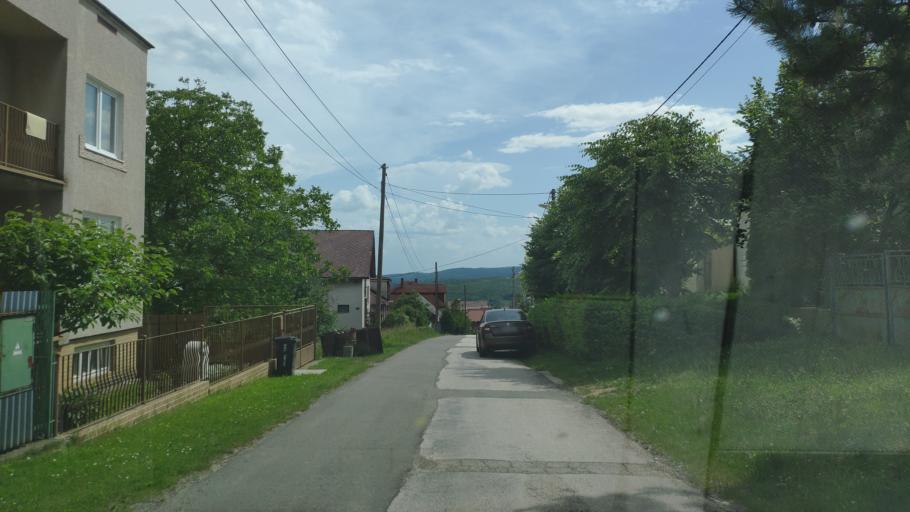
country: SK
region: Kosicky
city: Medzev
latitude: 48.7130
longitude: 20.9738
